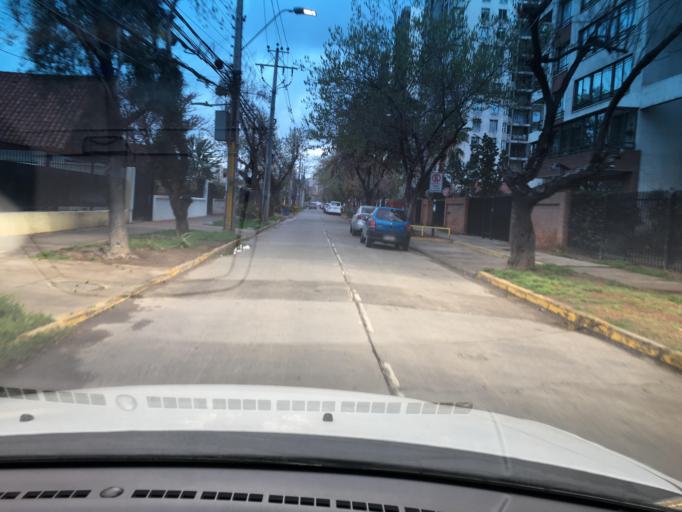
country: CL
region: Santiago Metropolitan
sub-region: Provincia de Santiago
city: Villa Presidente Frei, Nunoa, Santiago, Chile
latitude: -33.4874
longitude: -70.5979
